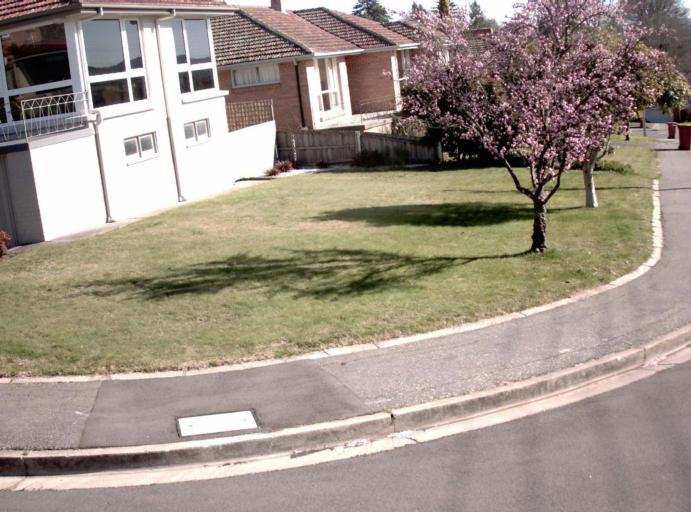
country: AU
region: Tasmania
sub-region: Launceston
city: Newstead
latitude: -41.4460
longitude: 147.1664
